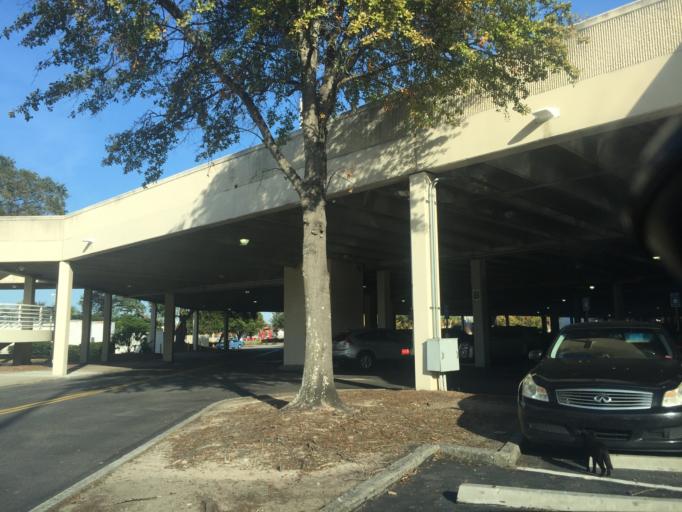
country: US
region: Georgia
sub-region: Chatham County
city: Isle of Hope
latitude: 32.0032
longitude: -81.1157
